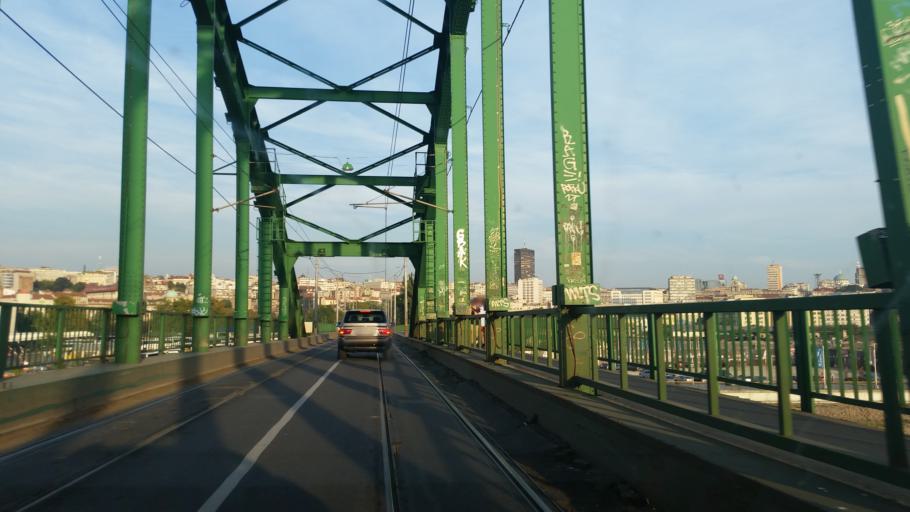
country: RS
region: Central Serbia
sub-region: Belgrade
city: Stari Grad
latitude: 44.8110
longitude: 20.4480
